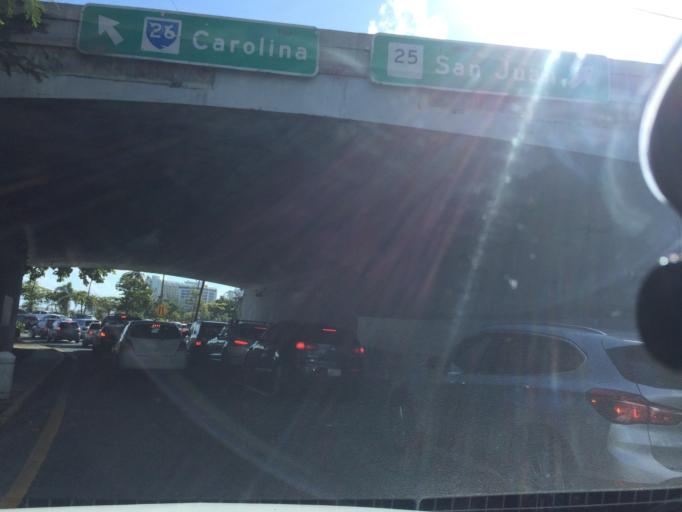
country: PR
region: San Juan
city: San Juan
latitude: 18.4575
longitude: -66.0868
